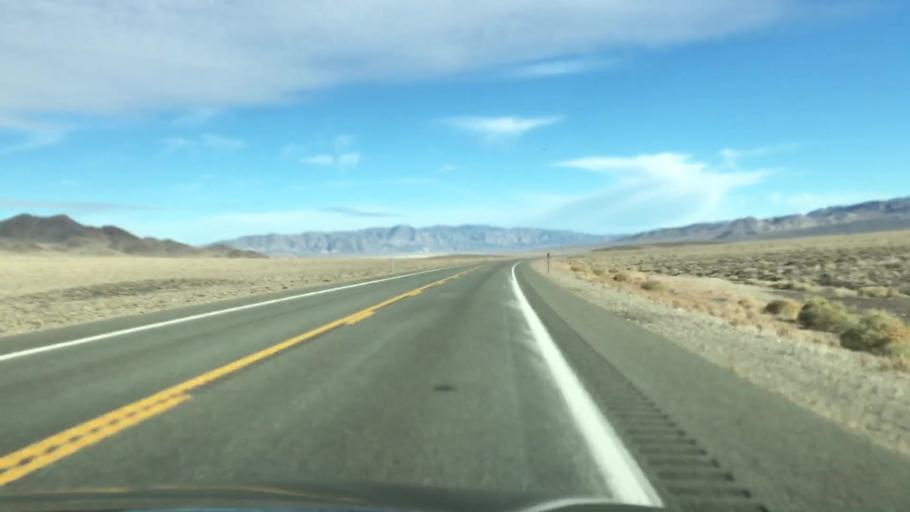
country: US
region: Nevada
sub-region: Mineral County
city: Hawthorne
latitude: 38.5495
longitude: -118.4344
